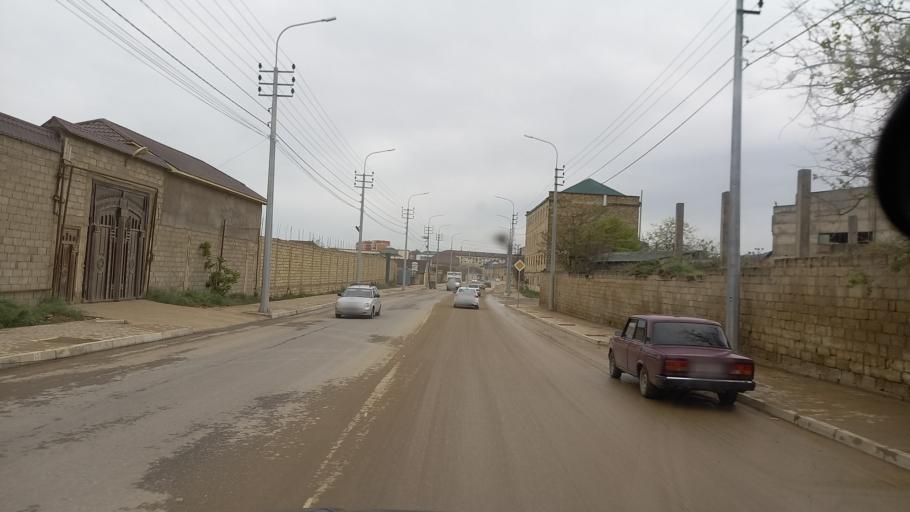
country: RU
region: Dagestan
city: Derbent
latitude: 42.0932
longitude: 48.2884
